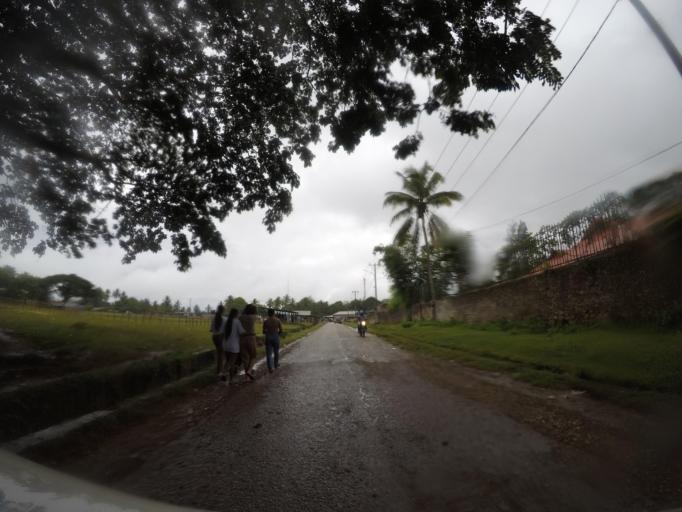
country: TL
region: Lautem
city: Lospalos
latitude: -8.5210
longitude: 126.9974
